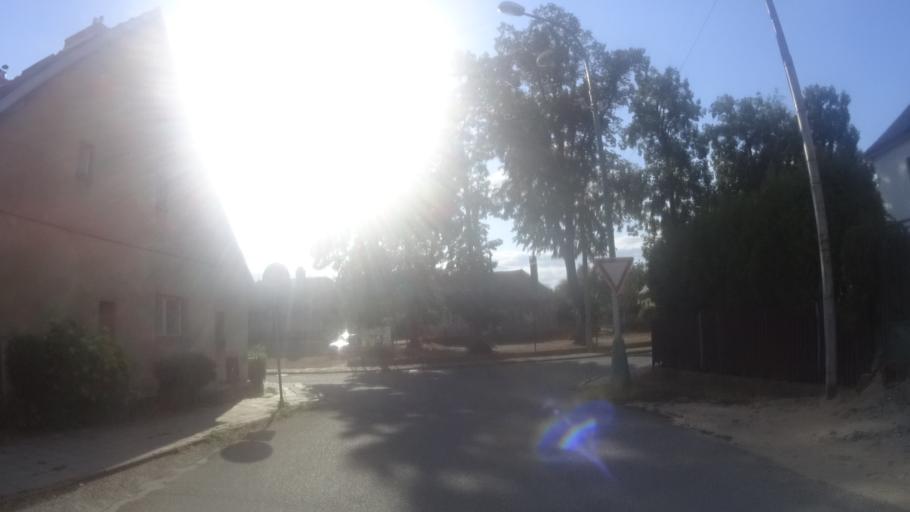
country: CZ
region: Kralovehradecky
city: Trebechovice pod Orebem
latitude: 50.1995
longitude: 15.9960
